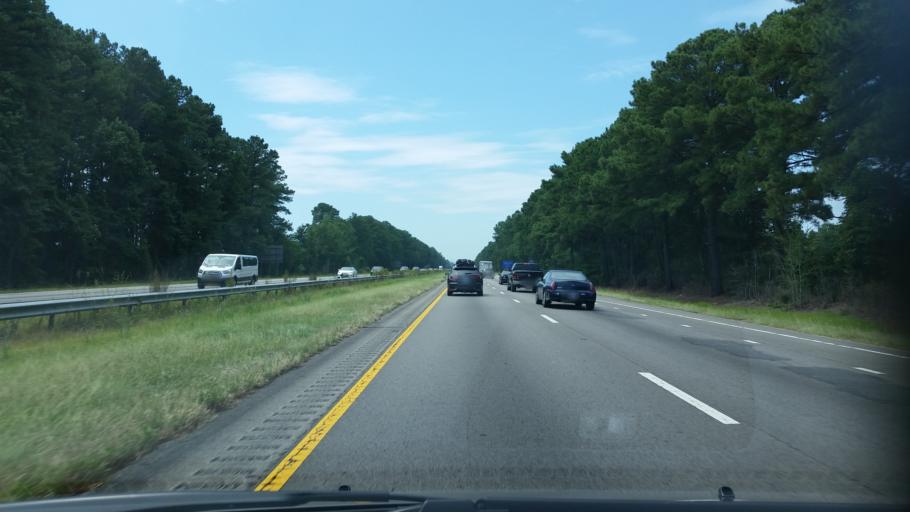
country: US
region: North Carolina
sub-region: Cumberland County
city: Eastover
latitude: 35.1561
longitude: -78.7195
